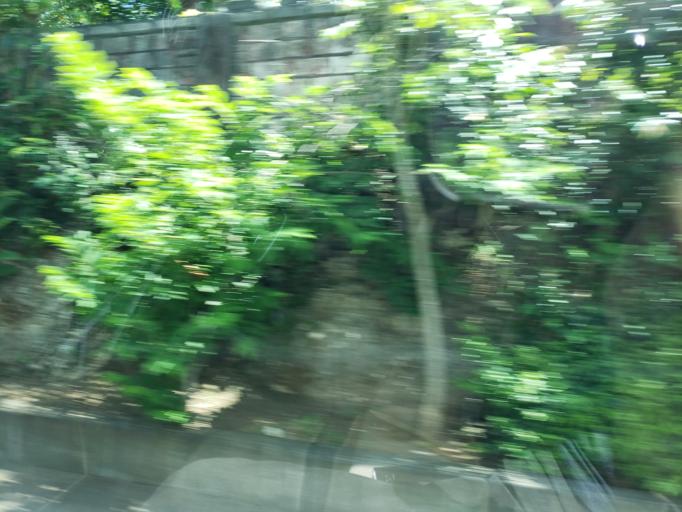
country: ID
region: Bali
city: Pecatu
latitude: -8.8416
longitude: 115.1223
